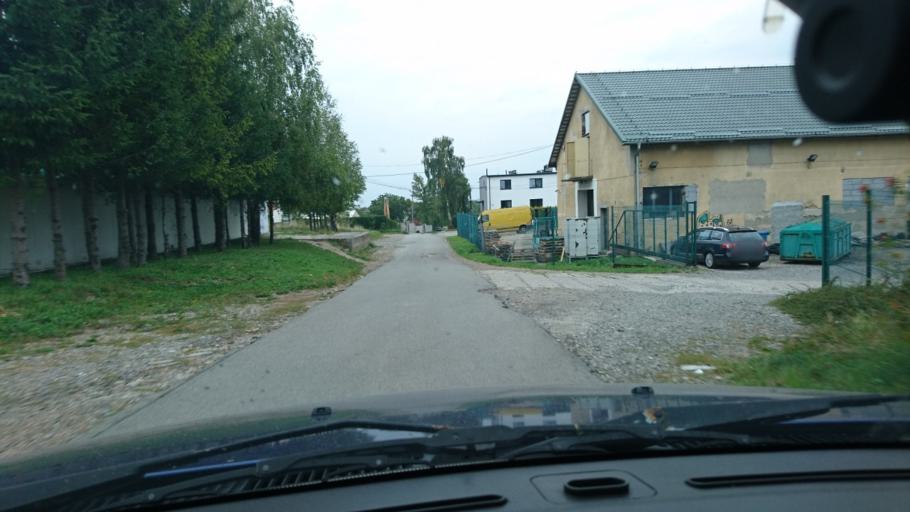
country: PL
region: Silesian Voivodeship
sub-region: Powiat bielski
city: Mazancowice
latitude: 49.8238
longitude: 18.9962
